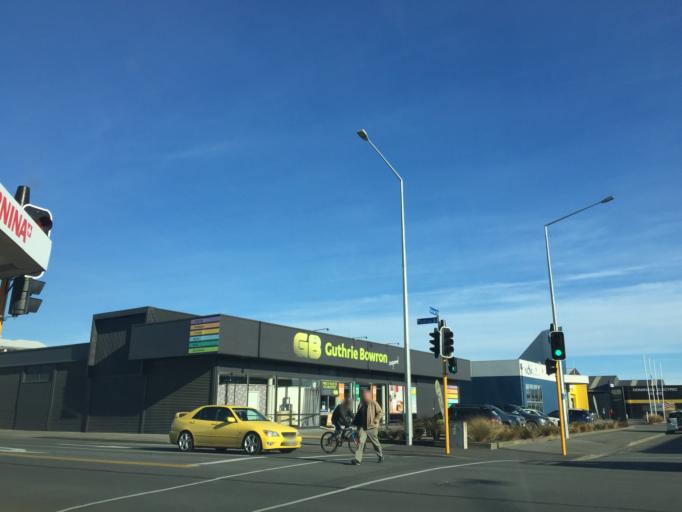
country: NZ
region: Southland
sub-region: Invercargill City
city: Invercargill
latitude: -46.4086
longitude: 168.3539
